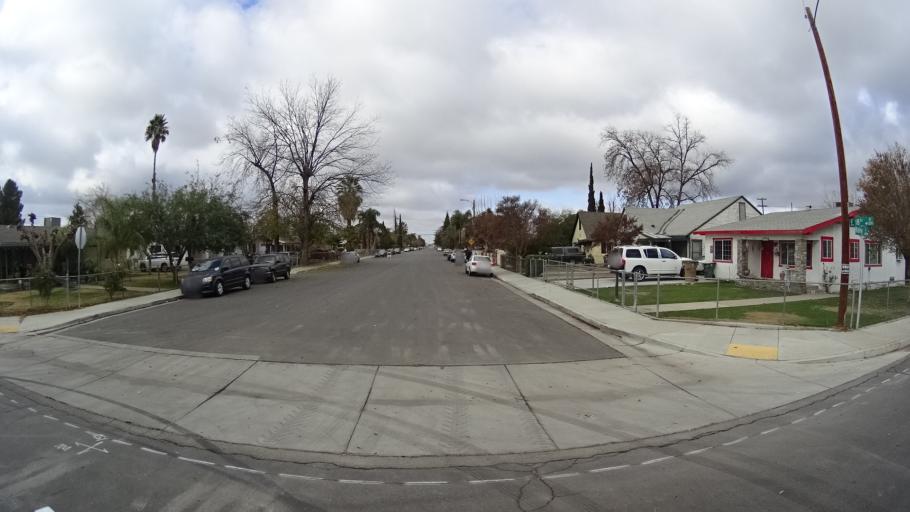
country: US
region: California
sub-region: Kern County
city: Bakersfield
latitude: 35.3712
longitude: -118.9832
